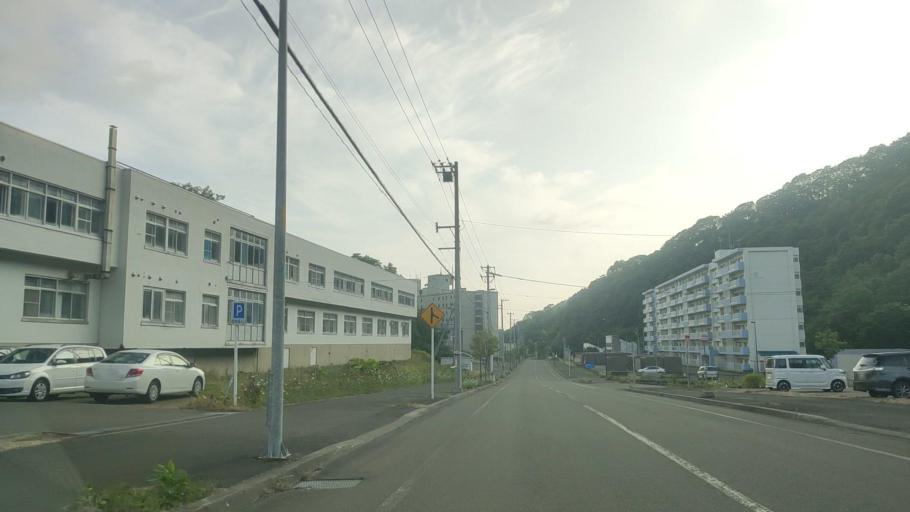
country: JP
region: Hokkaido
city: Iwamizawa
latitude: 43.0615
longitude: 141.9794
